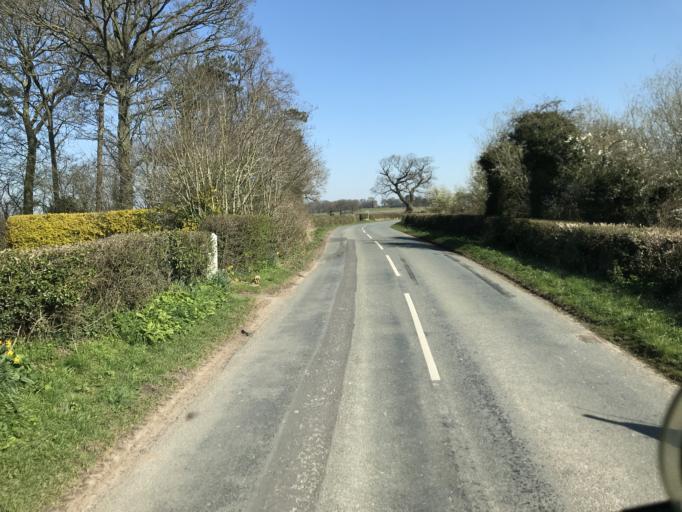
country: GB
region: England
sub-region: Cheshire West and Chester
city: Aldford
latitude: 53.1447
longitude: -2.8420
